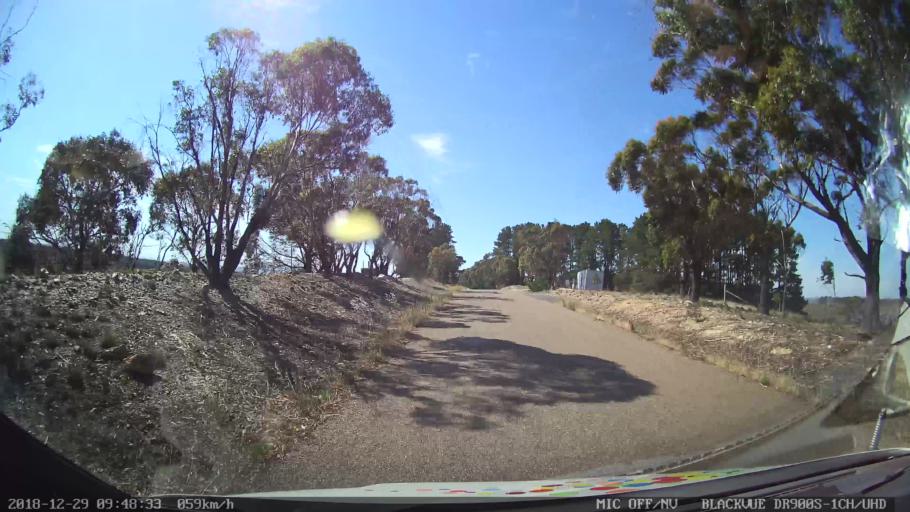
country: AU
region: New South Wales
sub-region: Upper Lachlan Shire
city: Crookwell
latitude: -34.7169
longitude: 149.4561
